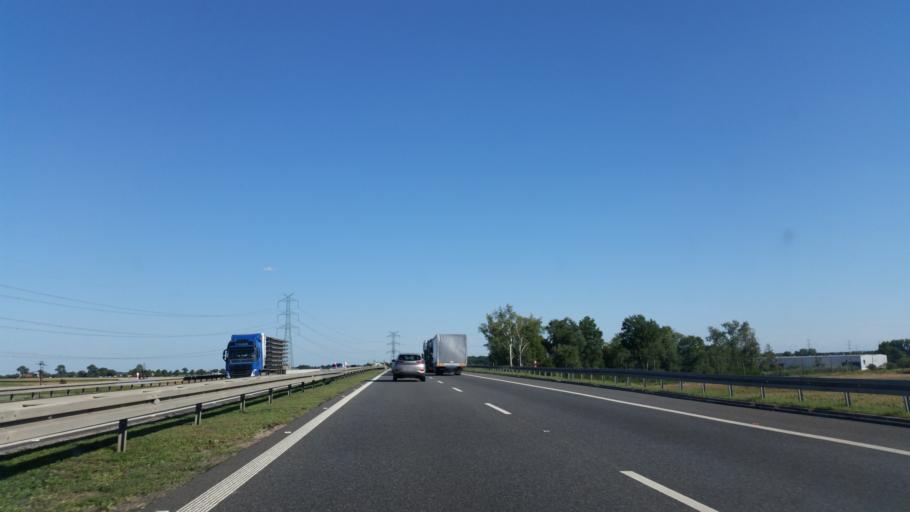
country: PL
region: Lower Silesian Voivodeship
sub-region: Powiat wroclawski
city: Zorawina
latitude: 50.9930
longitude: 17.0498
